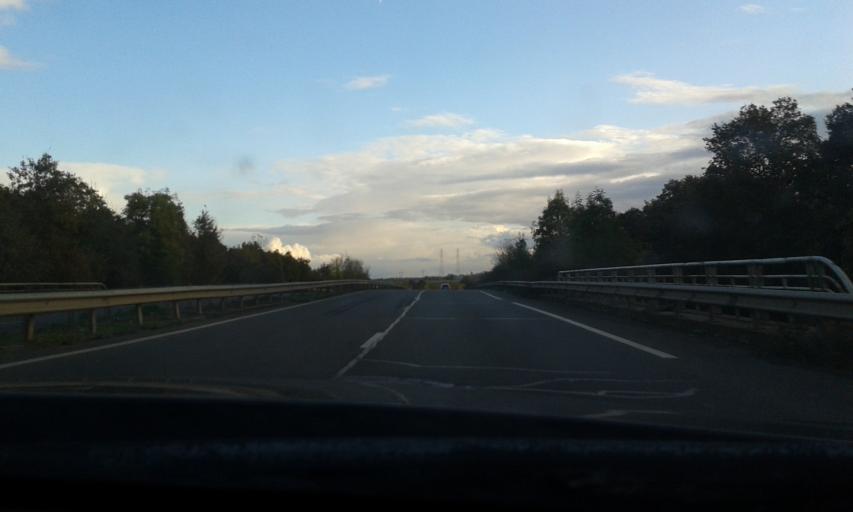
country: FR
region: Centre
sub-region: Departement d'Eure-et-Loir
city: Luce
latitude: 48.4267
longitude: 1.4341
